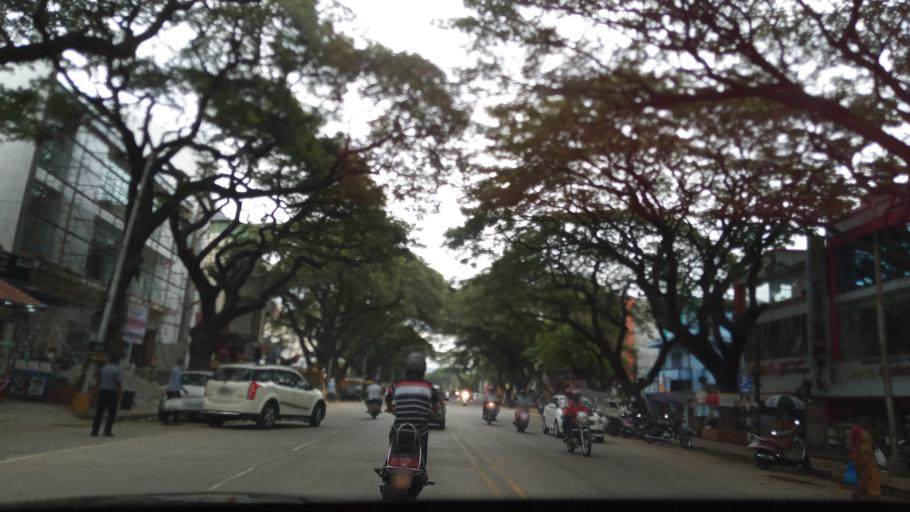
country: IN
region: Karnataka
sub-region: Mysore
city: Mysore
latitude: 12.3219
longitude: 76.6464
